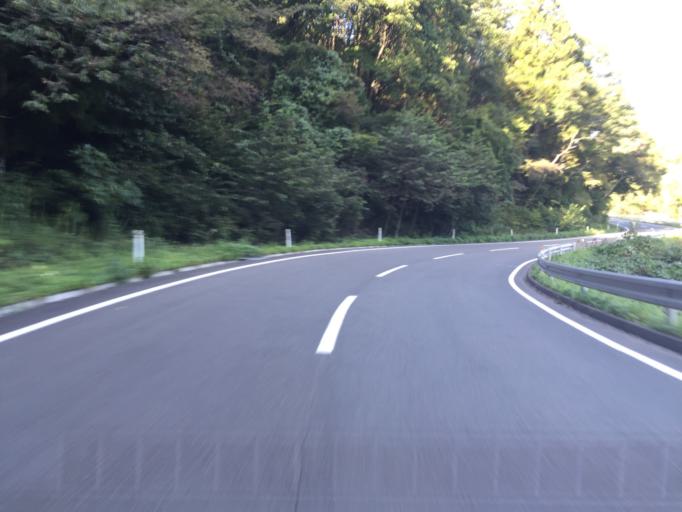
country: JP
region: Miyagi
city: Marumori
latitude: 37.8671
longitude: 140.7798
